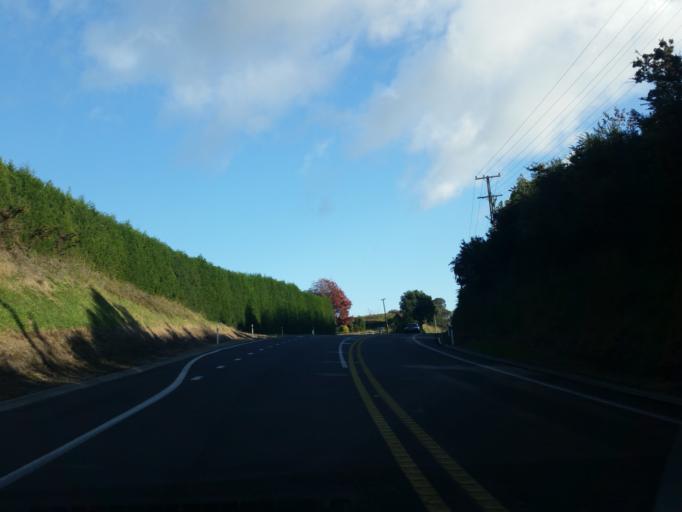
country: NZ
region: Bay of Plenty
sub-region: Tauranga City
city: Tauranga
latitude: -37.6964
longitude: 176.0515
